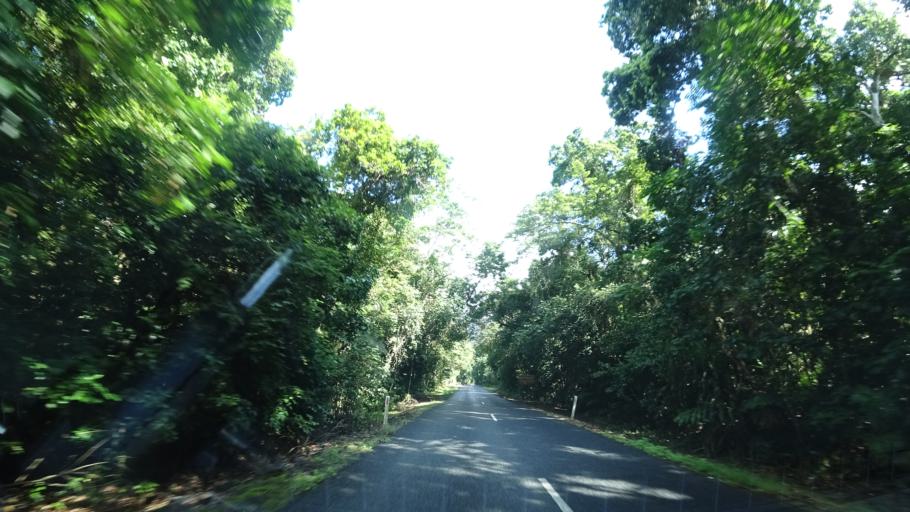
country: AU
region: Queensland
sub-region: Cairns
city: Port Douglas
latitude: -16.1378
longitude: 145.4399
